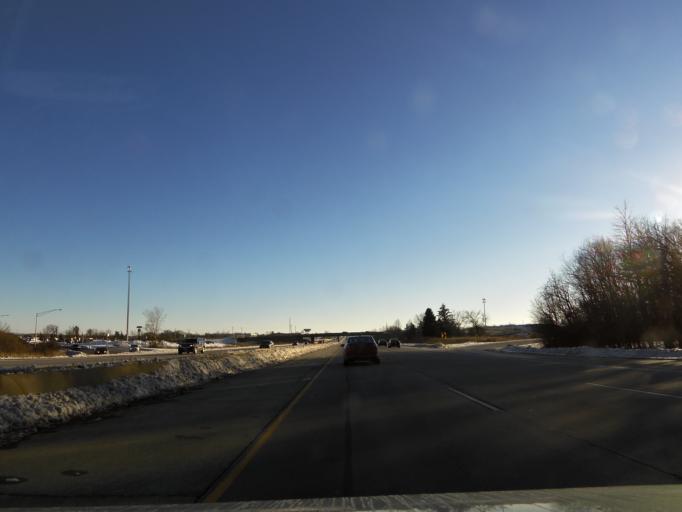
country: US
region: Wisconsin
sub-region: Racine County
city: Caledonia
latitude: 42.8762
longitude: -87.9372
